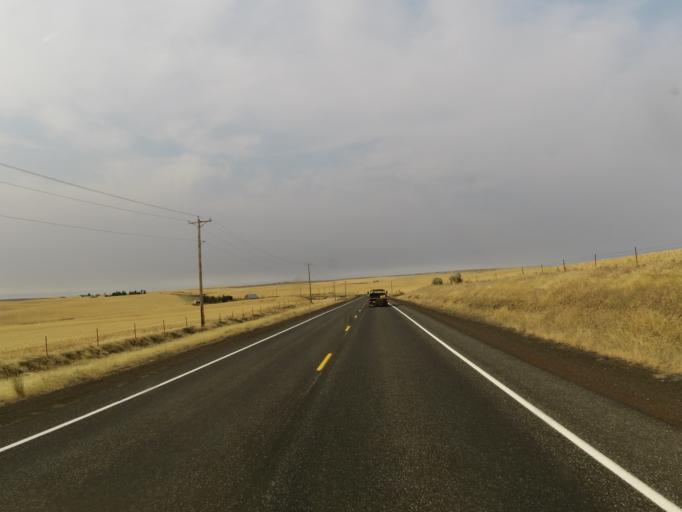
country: US
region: Oregon
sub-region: Sherman County
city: Moro
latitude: 45.4108
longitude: -120.7855
